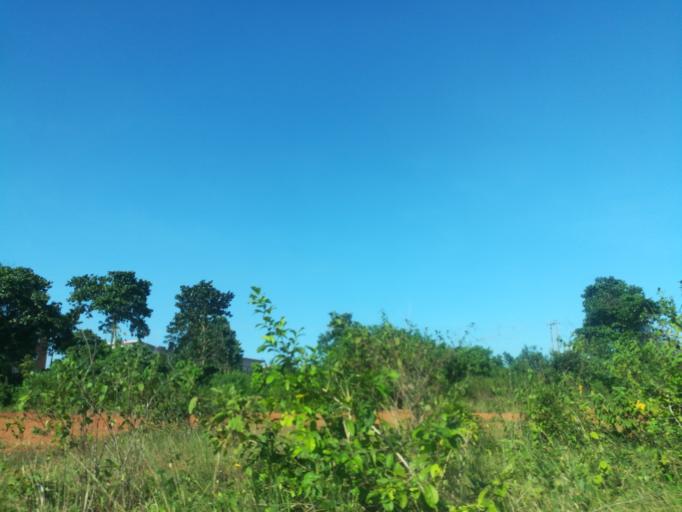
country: NG
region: Lagos
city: Ikorodu
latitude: 6.5616
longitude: 3.5353
